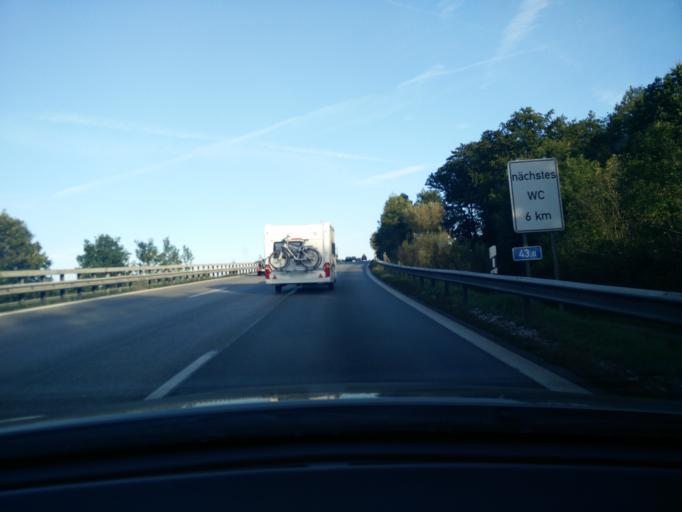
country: DE
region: Bavaria
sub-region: Upper Bavaria
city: Irschenberg
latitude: 47.8233
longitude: 11.9250
